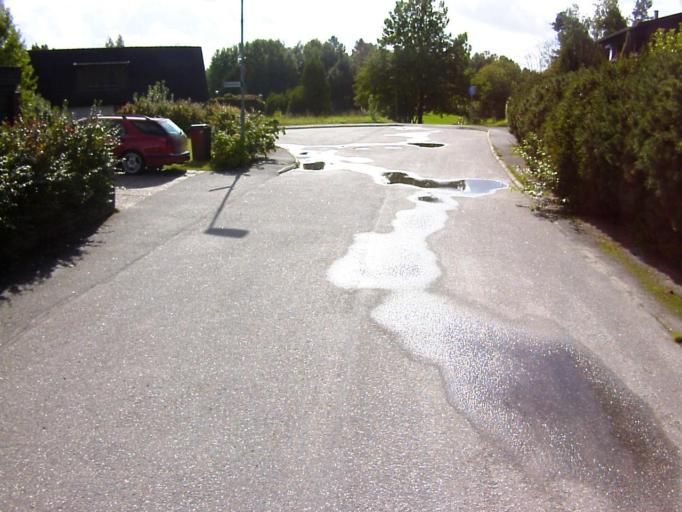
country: SE
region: Soedermanland
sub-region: Eskilstuna Kommun
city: Eskilstuna
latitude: 59.3968
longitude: 16.5336
